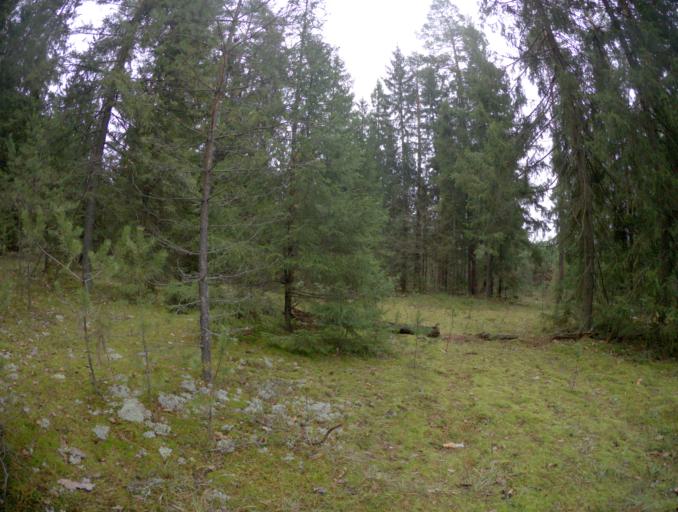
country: RU
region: Vladimir
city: Golovino
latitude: 56.0141
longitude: 40.5046
